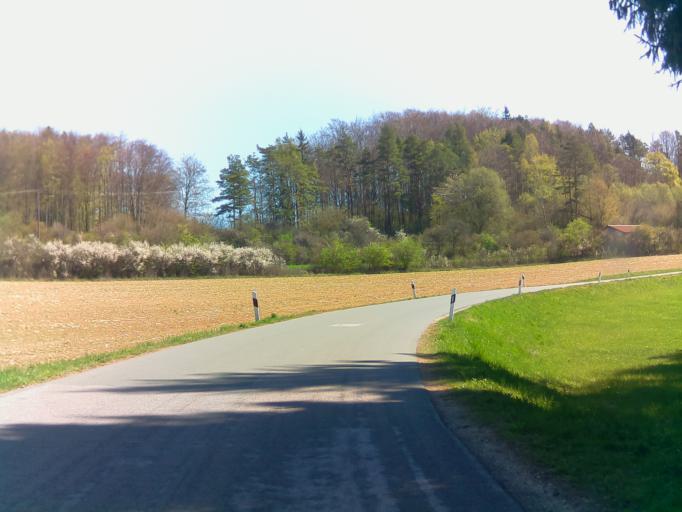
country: DE
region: Bavaria
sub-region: Upper Palatinate
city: Kastl
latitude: 49.4083
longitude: 11.6533
